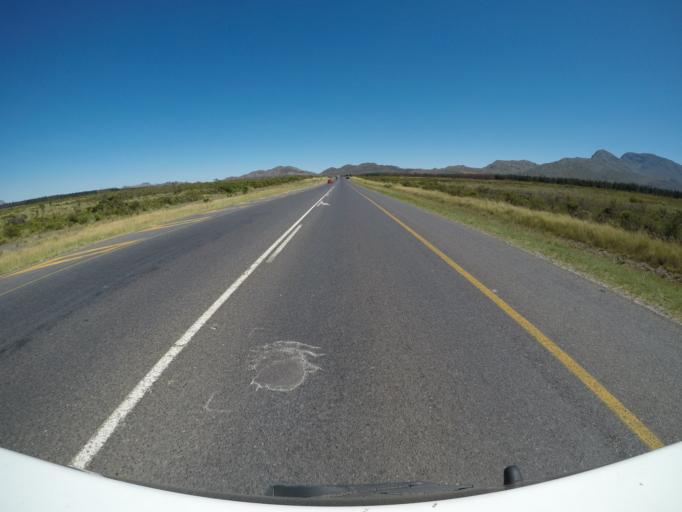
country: ZA
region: Western Cape
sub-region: Overberg District Municipality
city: Grabouw
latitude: -34.1569
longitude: 18.9725
